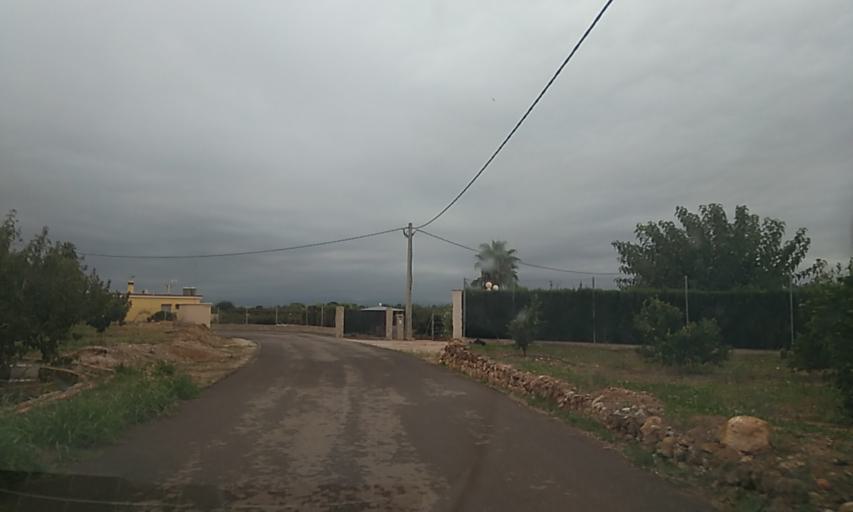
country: ES
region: Valencia
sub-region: Provincia de Valencia
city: Benimodo
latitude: 39.1913
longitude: -0.5582
